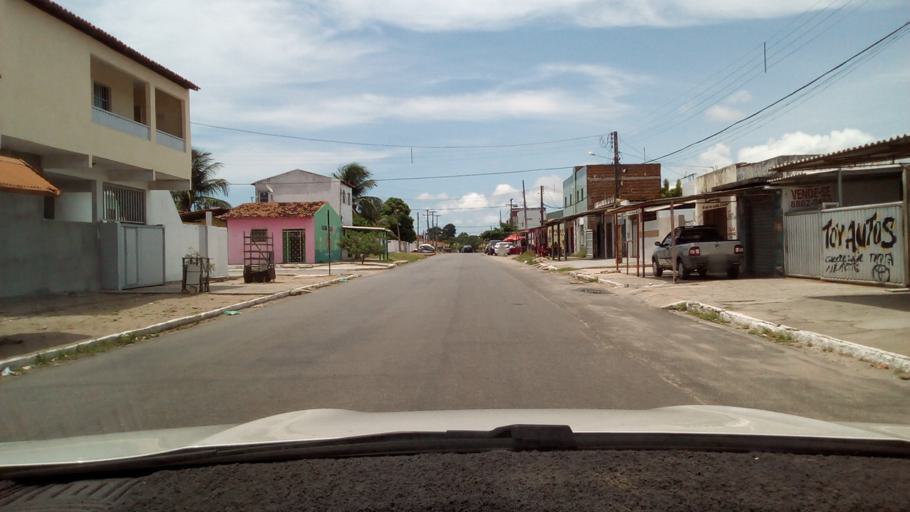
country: BR
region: Paraiba
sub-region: Joao Pessoa
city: Joao Pessoa
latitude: -7.1801
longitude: -34.8294
